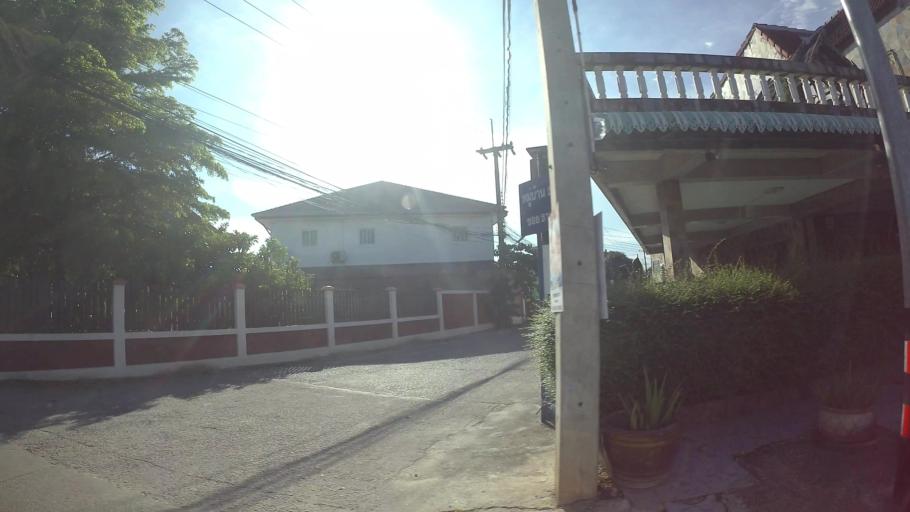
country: TH
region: Rayong
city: Rayong
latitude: 12.6729
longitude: 101.3009
